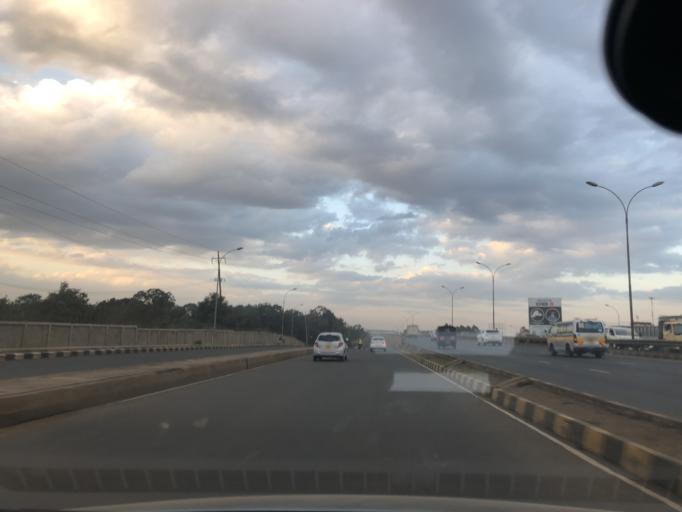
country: KE
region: Kiambu
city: Kiambu
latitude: -1.1905
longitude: 36.9292
